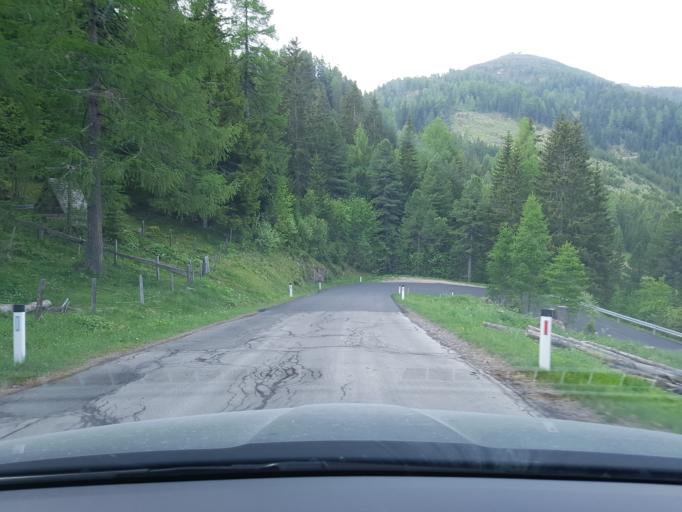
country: AT
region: Salzburg
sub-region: Politischer Bezirk Tamsweg
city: Thomatal
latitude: 46.9716
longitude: 13.7623
